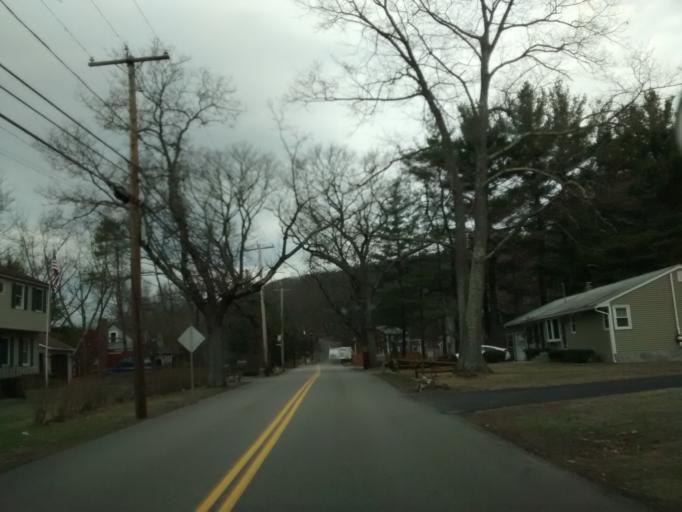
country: US
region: Massachusetts
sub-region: Worcester County
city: Grafton
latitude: 42.1996
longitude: -71.6929
